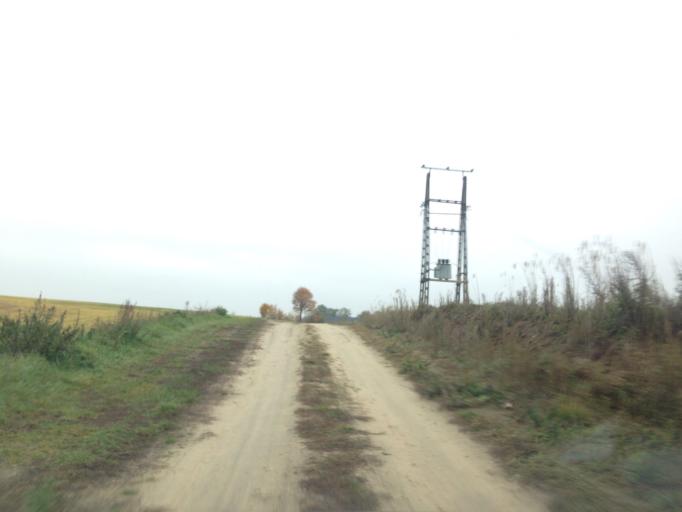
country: PL
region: Kujawsko-Pomorskie
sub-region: Powiat brodnicki
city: Gorzno
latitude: 53.2129
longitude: 19.6204
